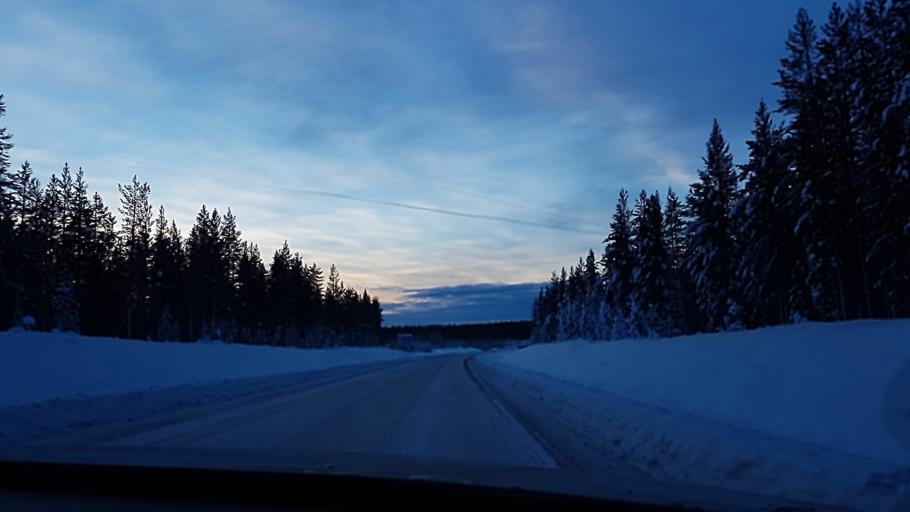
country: SE
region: Norrbotten
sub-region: Jokkmokks Kommun
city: Jokkmokk
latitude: 66.0669
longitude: 20.0768
